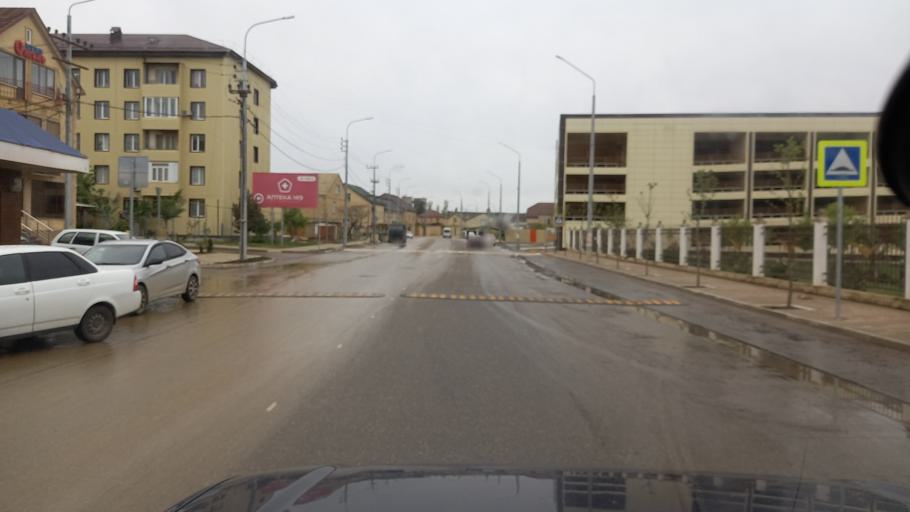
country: RU
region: Dagestan
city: Derbent
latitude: 42.0890
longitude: 48.2907
